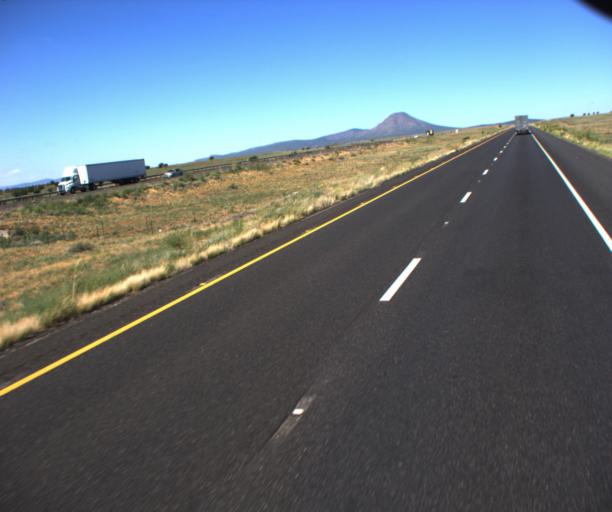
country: US
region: Arizona
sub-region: Yavapai County
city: Paulden
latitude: 35.2344
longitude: -112.6233
